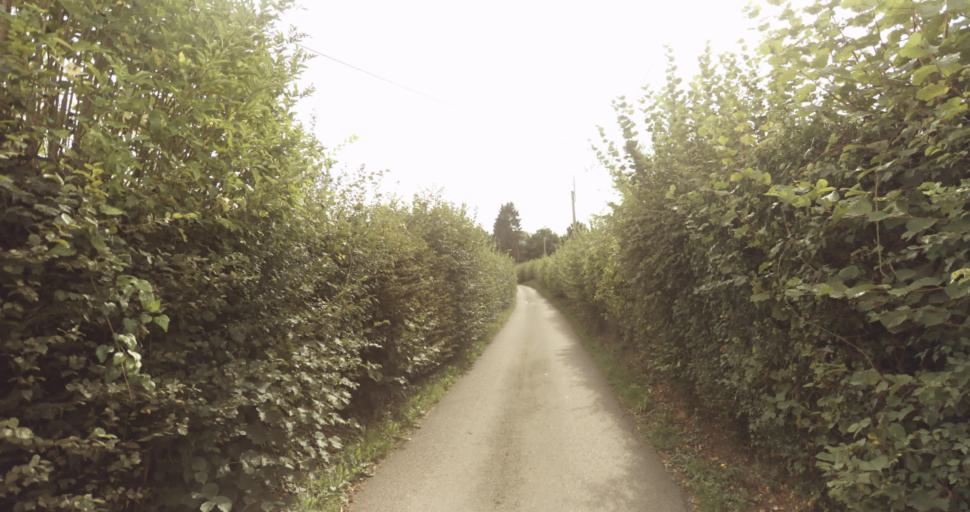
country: FR
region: Lower Normandy
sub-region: Departement de l'Orne
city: Gace
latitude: 48.8243
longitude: 0.2775
